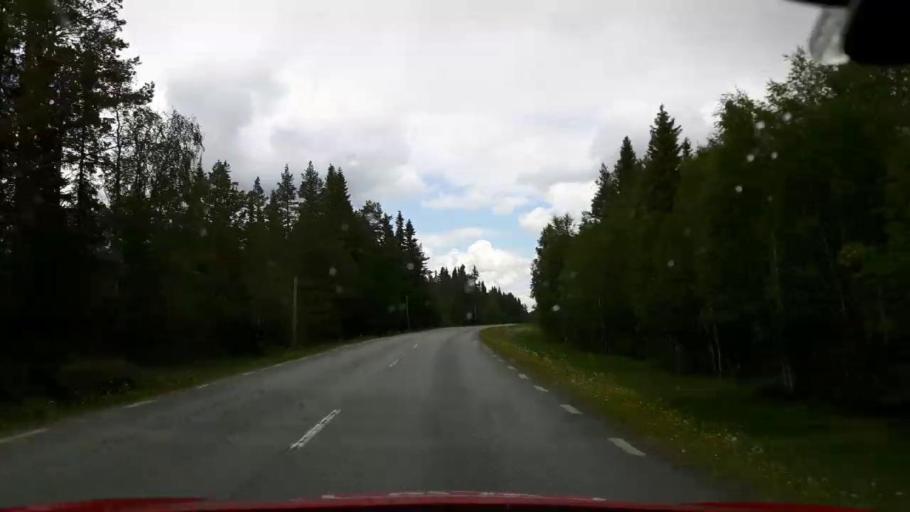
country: SE
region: Jaemtland
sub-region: Krokoms Kommun
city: Krokom
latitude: 63.5022
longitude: 14.2143
